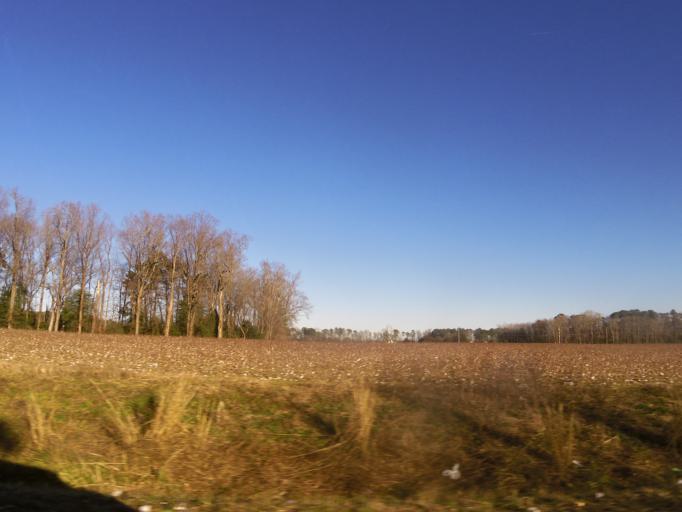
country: US
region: Virginia
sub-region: City of Franklin
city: Franklin
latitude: 36.6539
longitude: -76.8764
